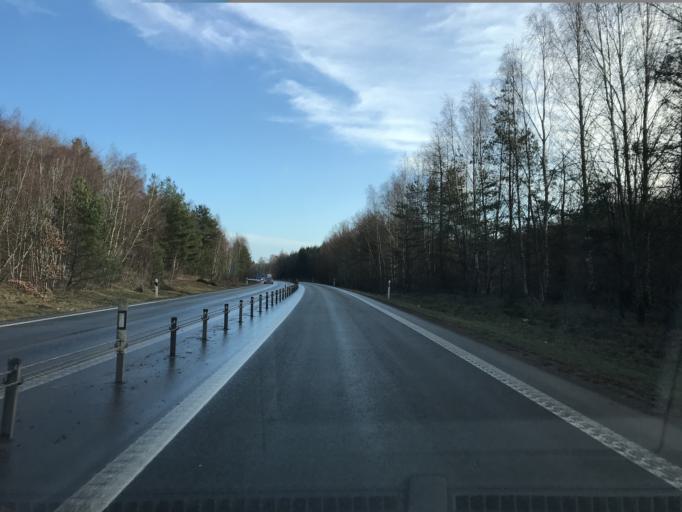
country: SE
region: Skane
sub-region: Hassleholms Kommun
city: Hassleholm
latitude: 56.1769
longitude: 13.7156
